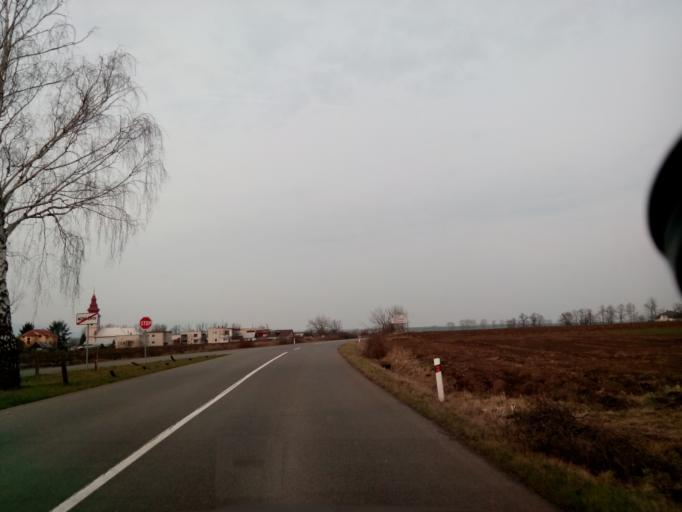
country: SK
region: Kosicky
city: Trebisov
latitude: 48.5785
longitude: 21.6406
